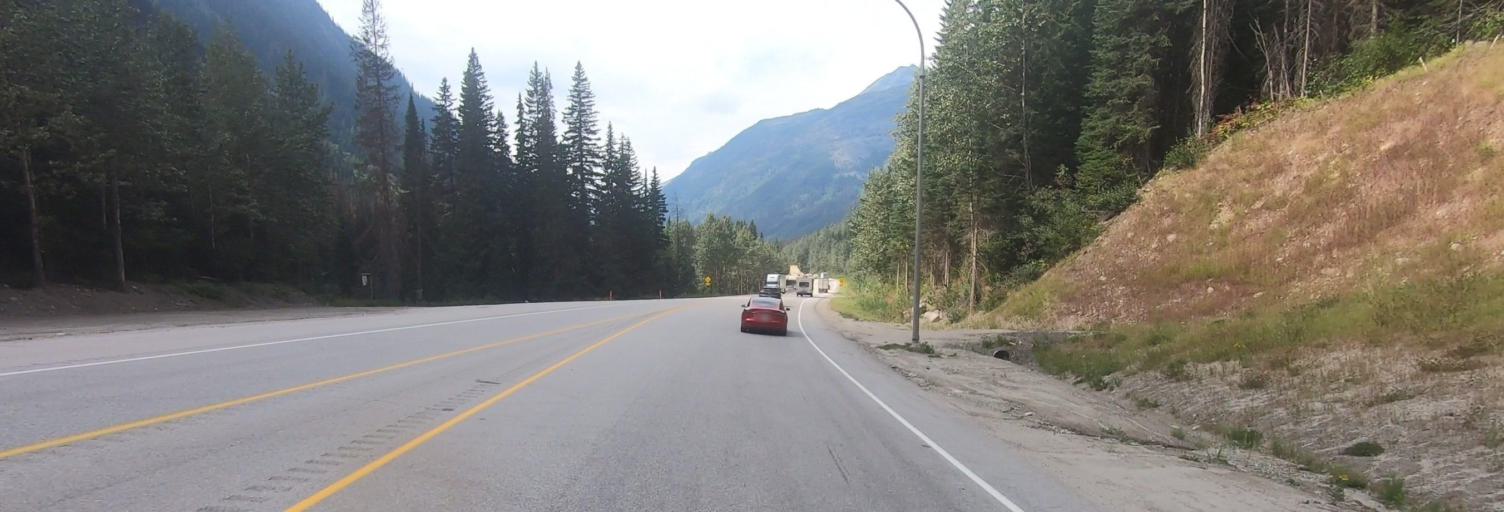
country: CA
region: British Columbia
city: Golden
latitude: 51.3227
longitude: -117.4836
